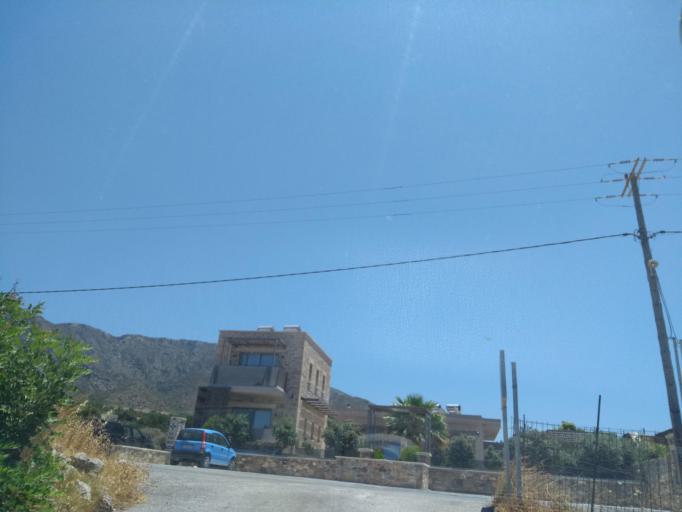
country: GR
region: Crete
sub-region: Nomos Chanias
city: Vryses
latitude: 35.3121
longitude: 23.5384
